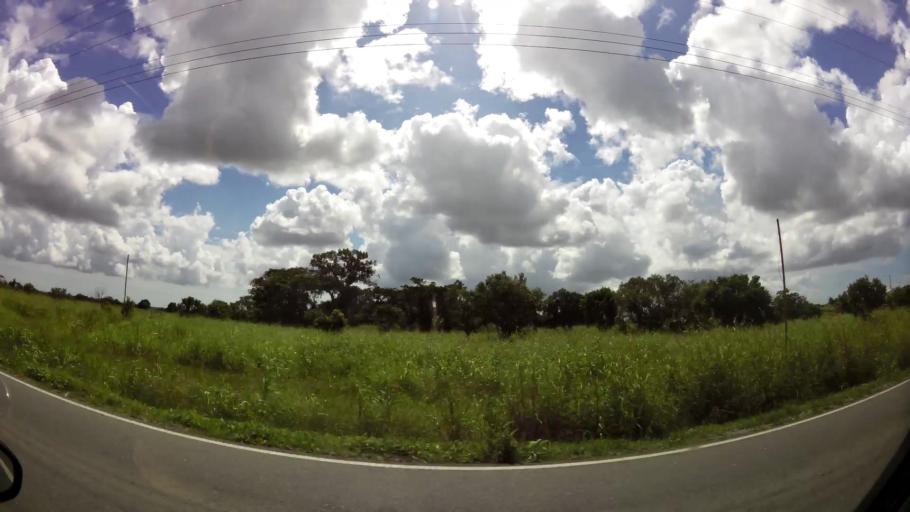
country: TT
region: Penal/Debe
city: Debe
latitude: 10.2233
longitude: -61.4799
